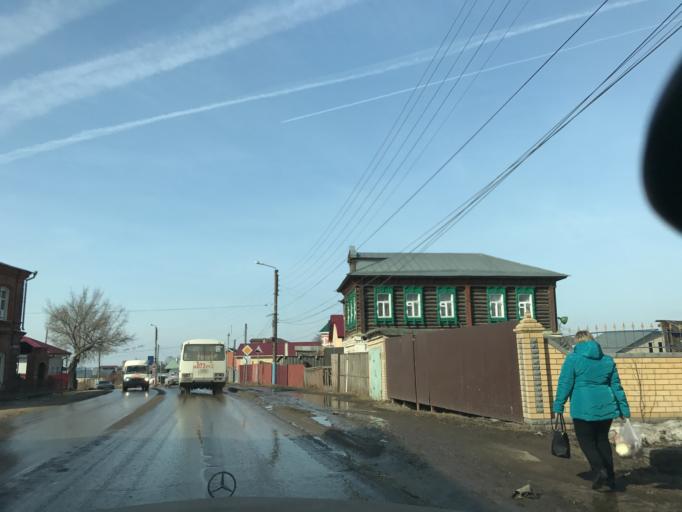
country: RU
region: Nizjnij Novgorod
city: Pavlovo
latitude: 55.9657
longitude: 43.0790
